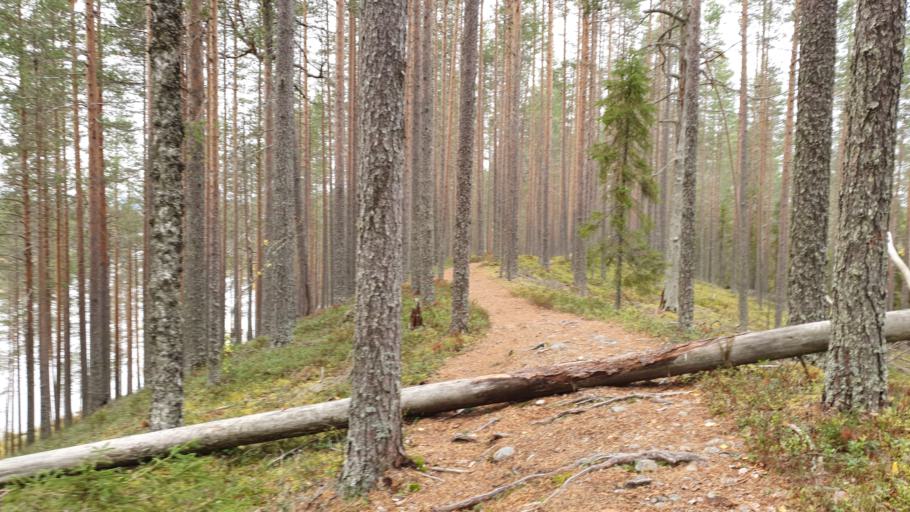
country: FI
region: Kainuu
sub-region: Kehys-Kainuu
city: Kuhmo
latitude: 64.2933
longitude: 29.3920
